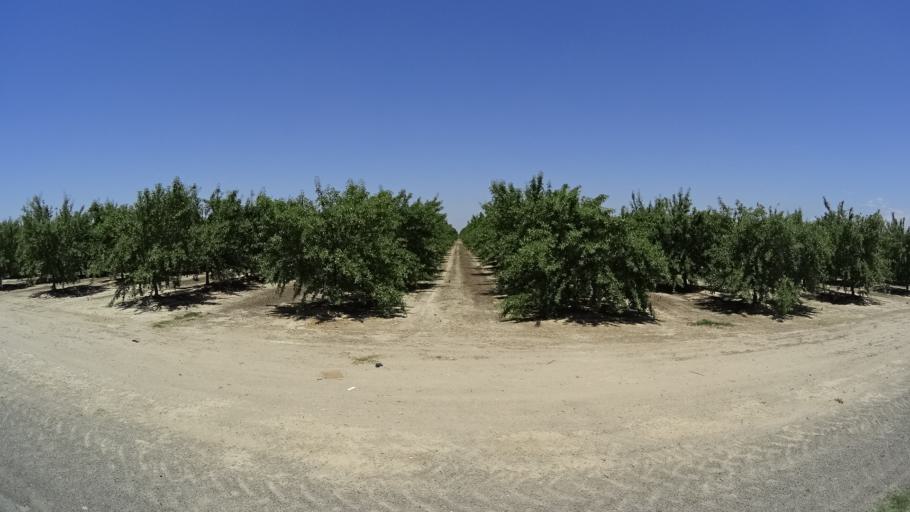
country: US
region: California
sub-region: Fresno County
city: Kingsburg
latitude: 36.4306
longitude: -119.5322
